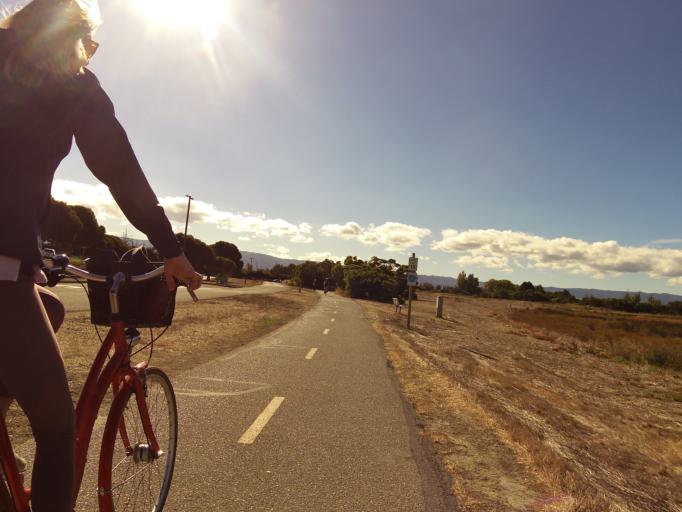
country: US
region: California
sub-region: Santa Clara County
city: Mountain View
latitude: 37.4336
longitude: -122.0826
